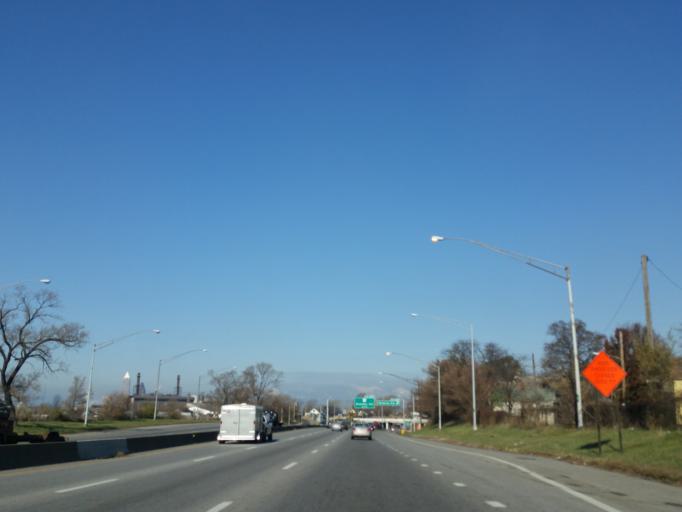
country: US
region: Ohio
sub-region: Cuyahoga County
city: Newburgh Heights
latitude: 41.4671
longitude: -81.6584
